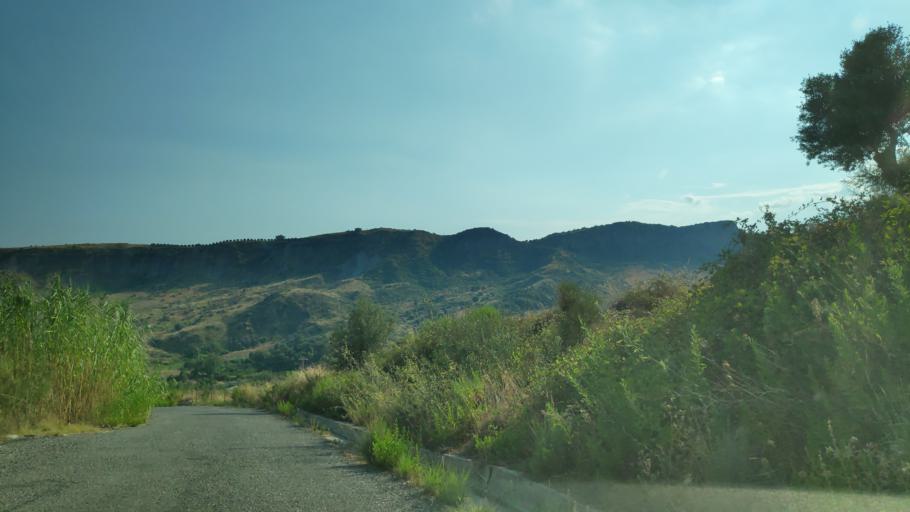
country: IT
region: Calabria
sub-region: Provincia di Reggio Calabria
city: Placanica
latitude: 38.4152
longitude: 16.4450
